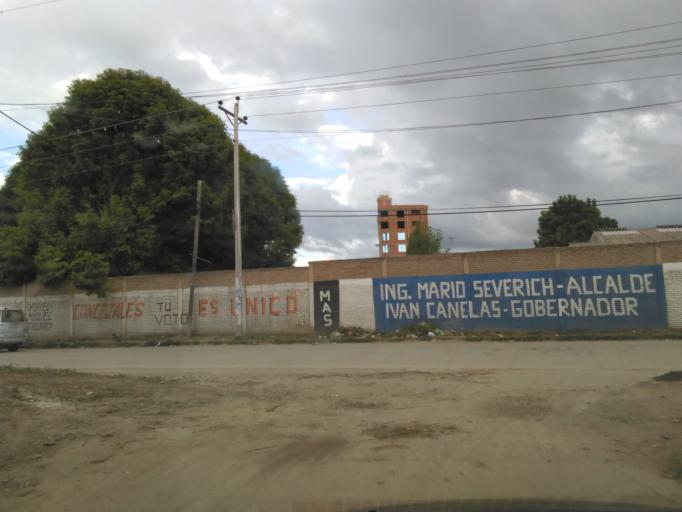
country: BO
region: Cochabamba
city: Cochabamba
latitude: -17.3928
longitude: -66.2304
